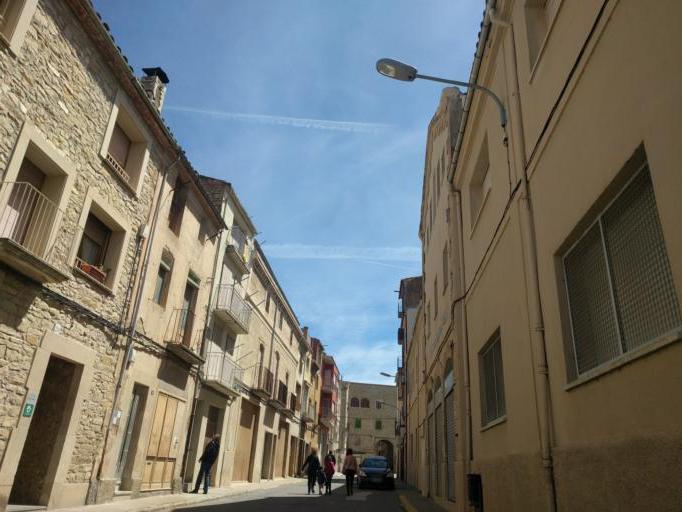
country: ES
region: Catalonia
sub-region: Provincia de Tarragona
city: Santa Coloma de Queralt
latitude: 41.5318
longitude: 1.3818
